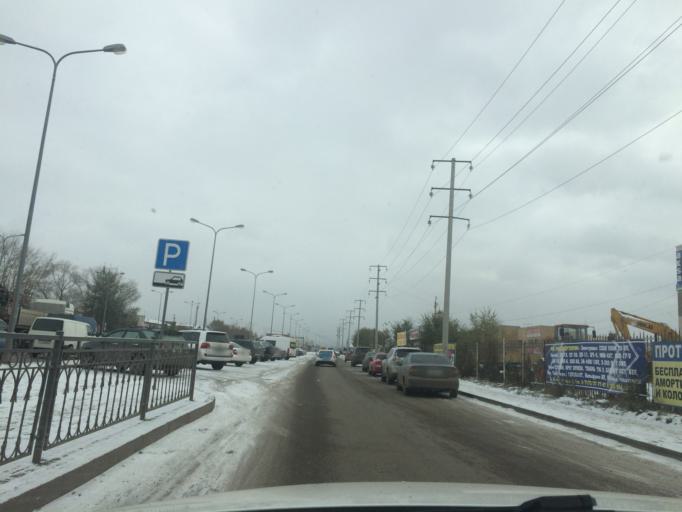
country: KZ
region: Astana Qalasy
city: Astana
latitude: 51.1799
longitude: 71.4647
